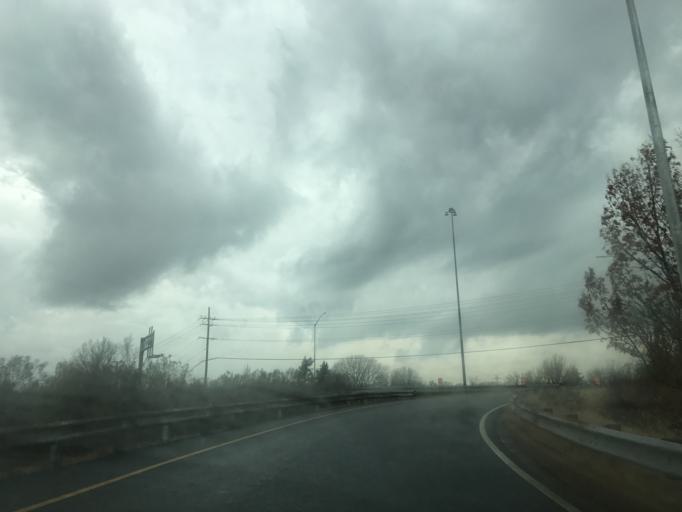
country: US
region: Maryland
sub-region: Baltimore County
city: Rosedale
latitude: 39.2963
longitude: -76.5024
